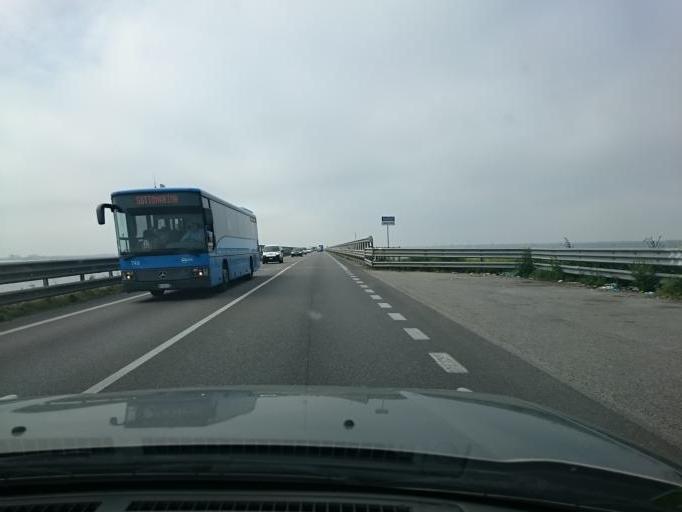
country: IT
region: Veneto
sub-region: Provincia di Venezia
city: Chioggia
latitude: 45.2049
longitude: 12.2502
